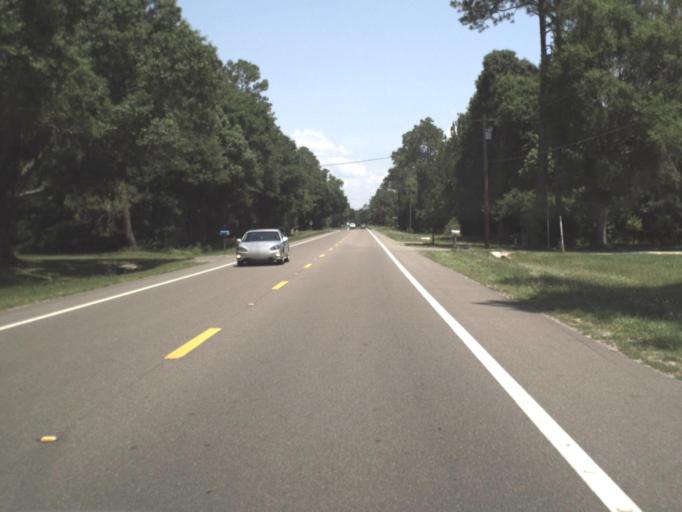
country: US
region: Florida
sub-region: Bradford County
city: Starke
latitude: 29.9090
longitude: -82.0920
